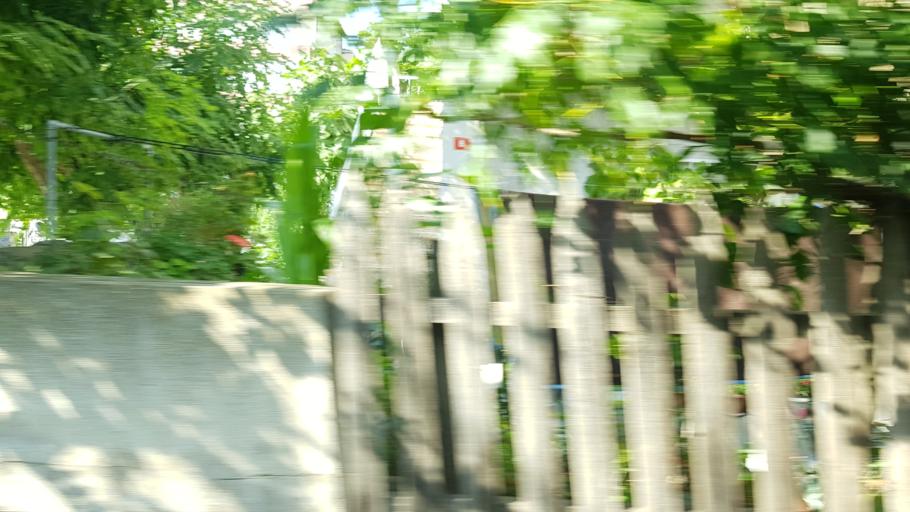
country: TR
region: Istanbul
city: Maltepe
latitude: 40.9057
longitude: 29.1964
